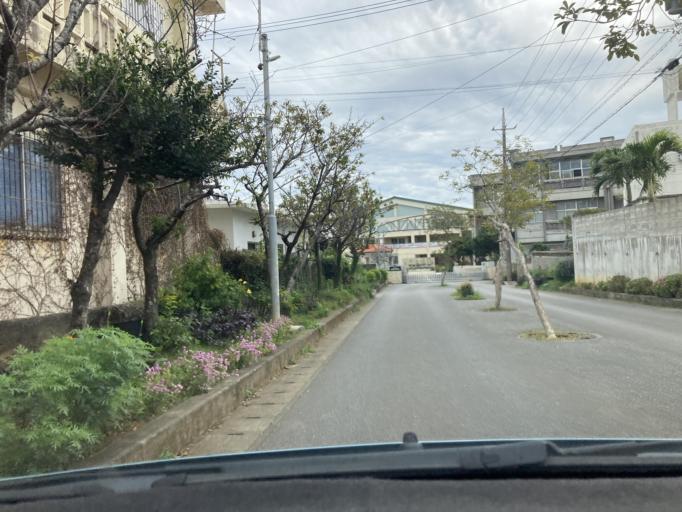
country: JP
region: Okinawa
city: Okinawa
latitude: 26.3817
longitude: 127.7525
